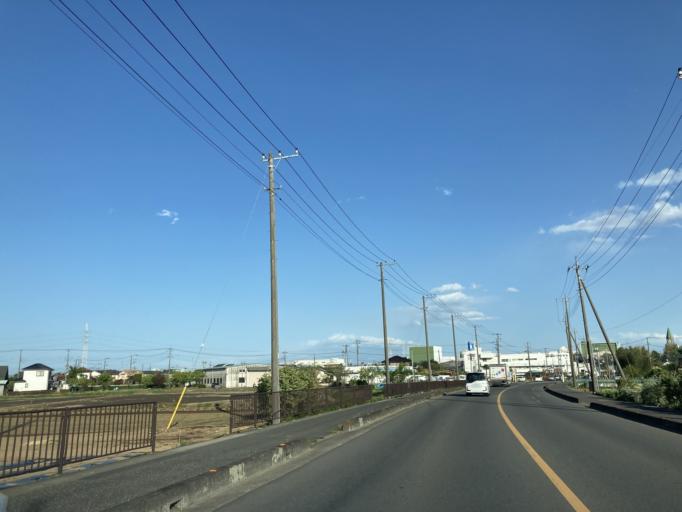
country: JP
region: Saitama
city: Sayama
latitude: 35.8835
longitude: 139.4265
